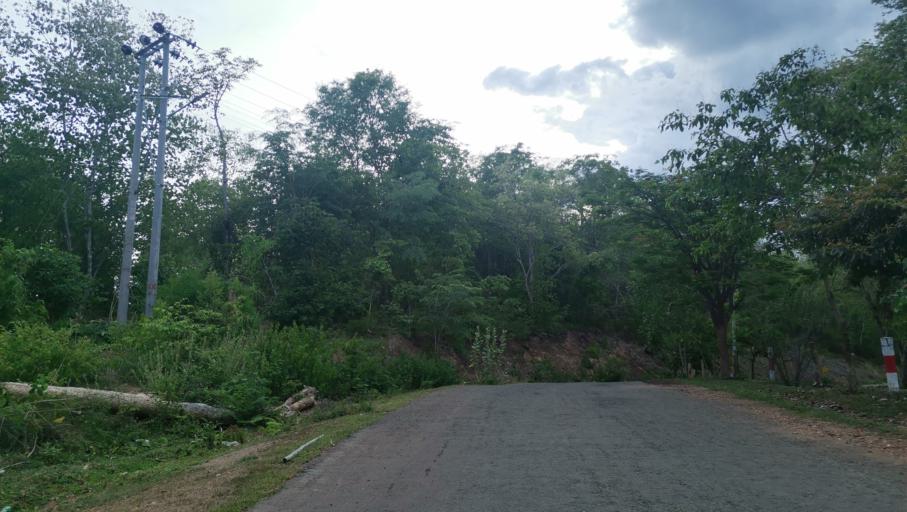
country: MM
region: Magway
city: Minbu
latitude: 20.0884
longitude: 94.5694
